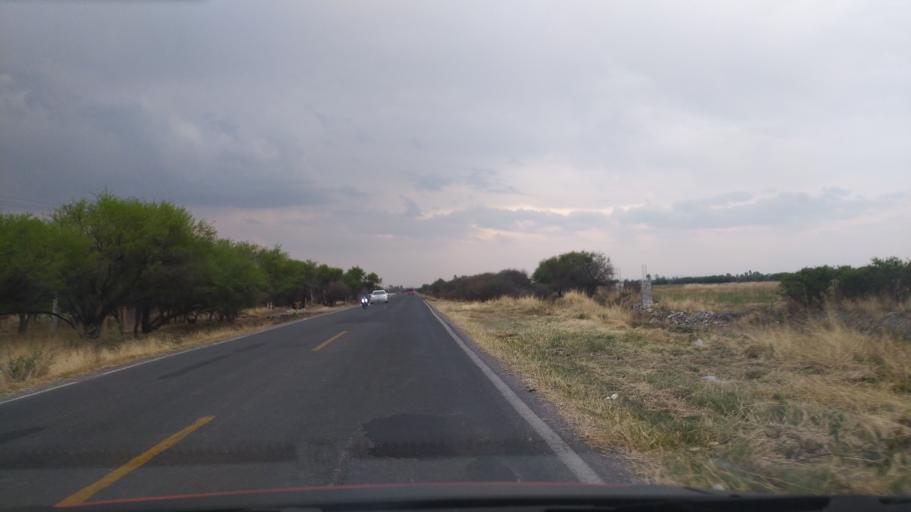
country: MX
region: Guanajuato
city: Ciudad Manuel Doblado
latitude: 20.7736
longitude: -101.9121
